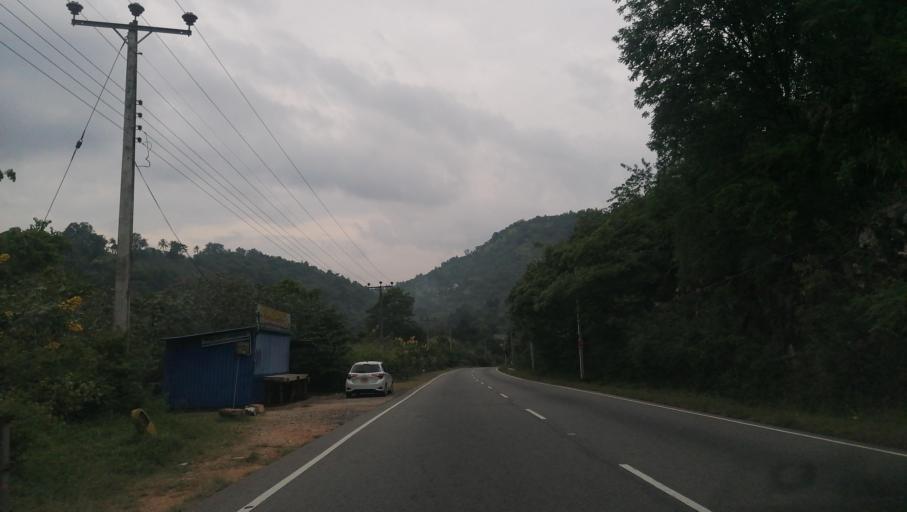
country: LK
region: Central
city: Kandy
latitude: 7.2457
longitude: 80.7280
